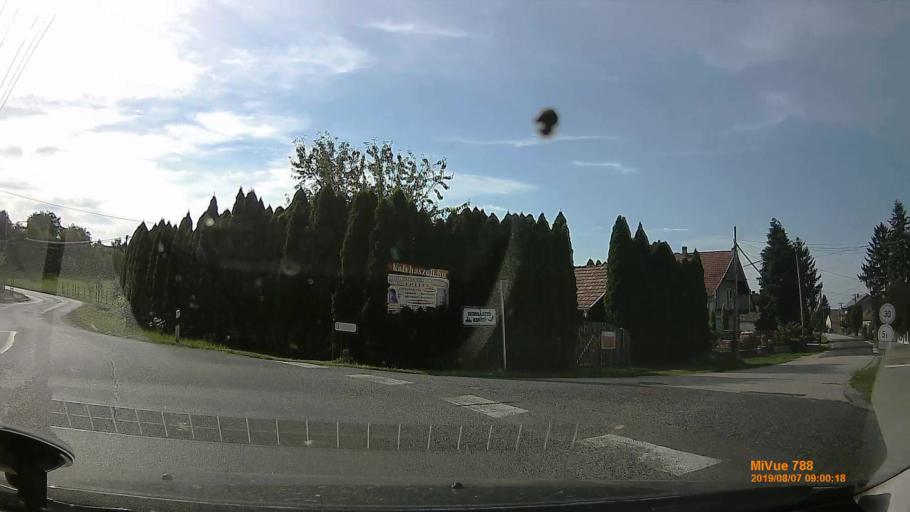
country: HU
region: Zala
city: Pacsa
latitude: 46.7290
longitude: 16.9457
